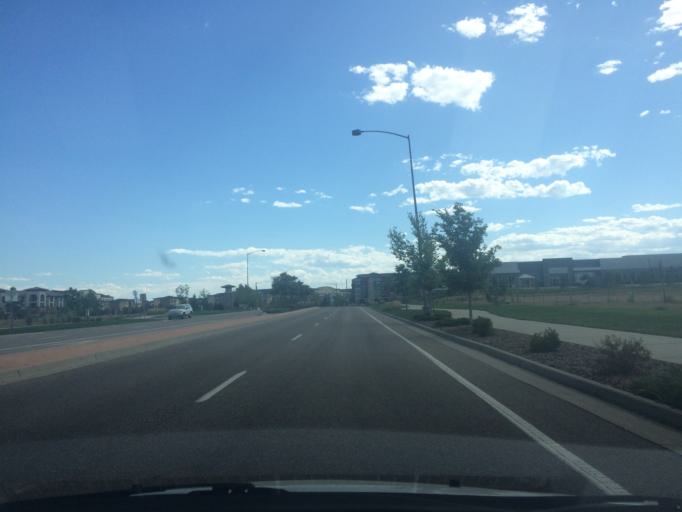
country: US
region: Colorado
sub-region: Boulder County
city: Louisville
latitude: 39.9464
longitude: -105.1236
